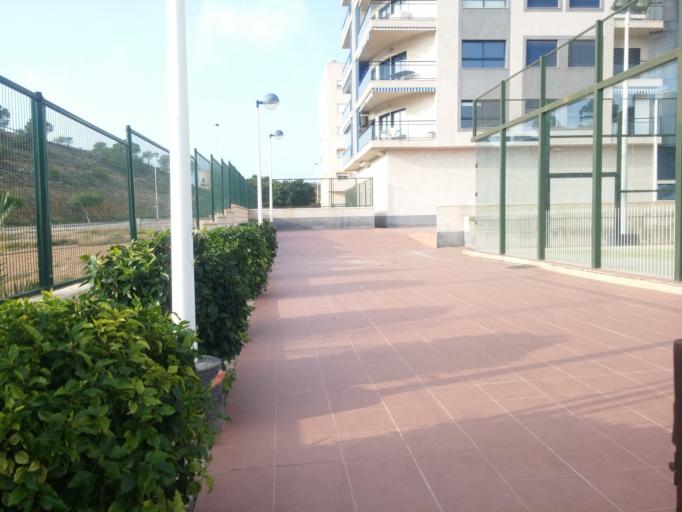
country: ES
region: Valencia
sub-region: Provincia de Alicante
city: Villajoyosa
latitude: 38.5010
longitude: -0.2439
